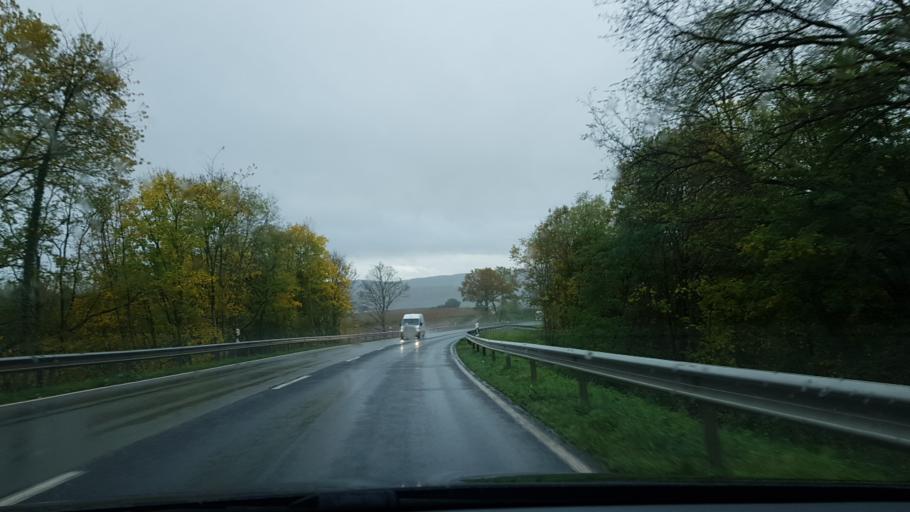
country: DE
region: Rheinland-Pfalz
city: Salmtal
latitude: 49.9413
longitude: 6.8495
